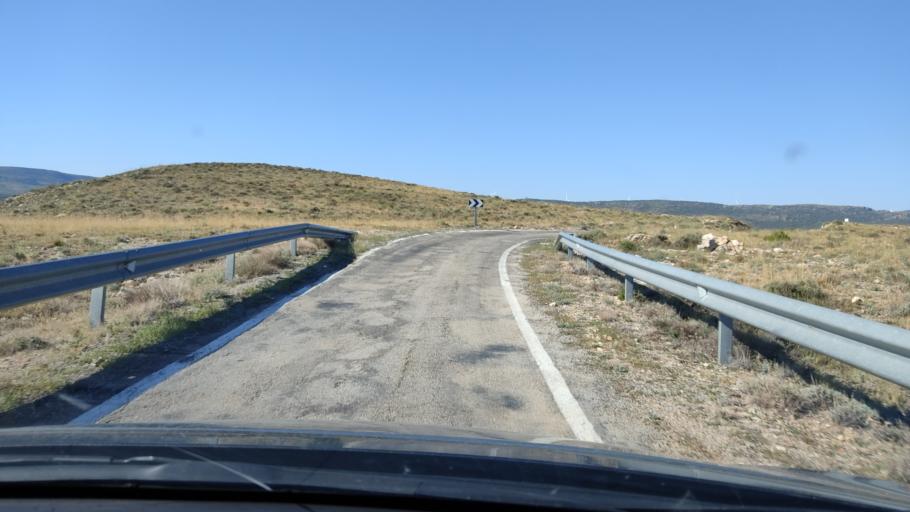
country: ES
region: Aragon
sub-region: Provincia de Teruel
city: Anadon
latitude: 41.0195
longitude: -0.9643
